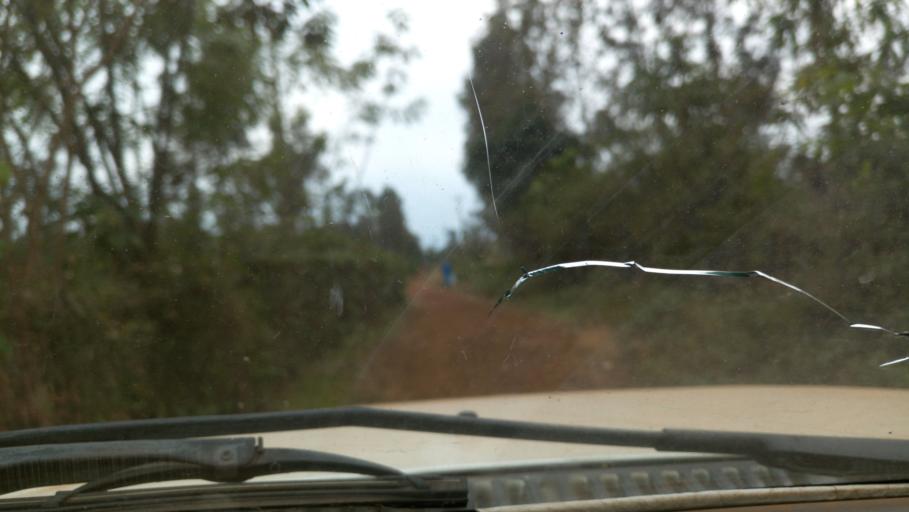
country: KE
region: Murang'a District
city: Maragua
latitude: -0.8719
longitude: 37.1880
